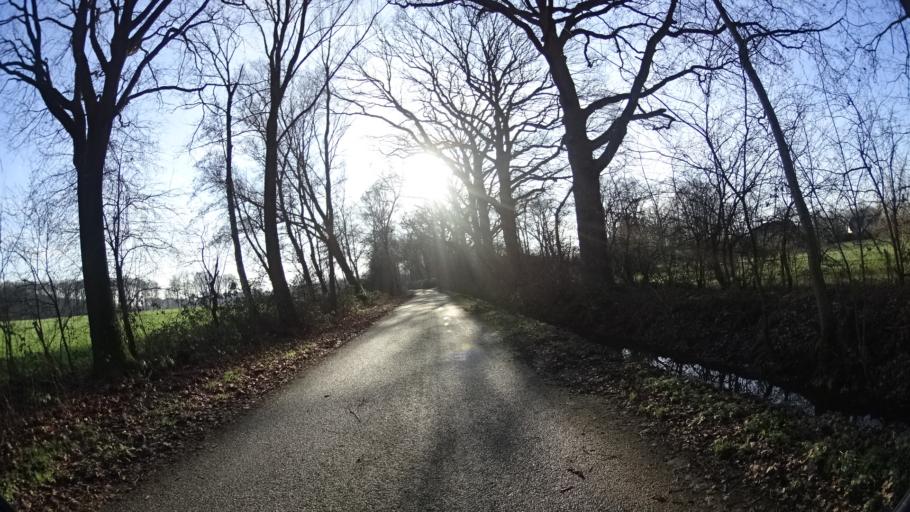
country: NL
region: Gelderland
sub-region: Gemeente Ede
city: Otterlo
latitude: 52.0476
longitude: 5.7321
